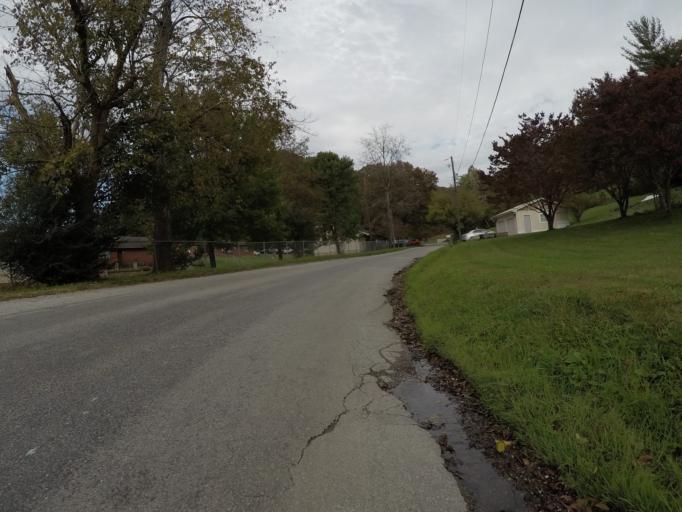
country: US
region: West Virginia
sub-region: Wayne County
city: Lavalette
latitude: 38.3378
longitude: -82.4483
